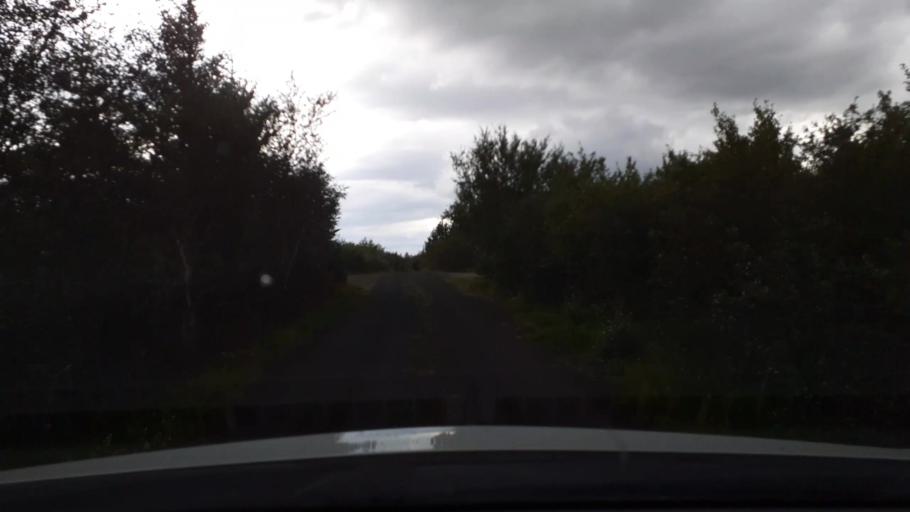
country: IS
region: West
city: Borgarnes
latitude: 64.6403
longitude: -21.7138
